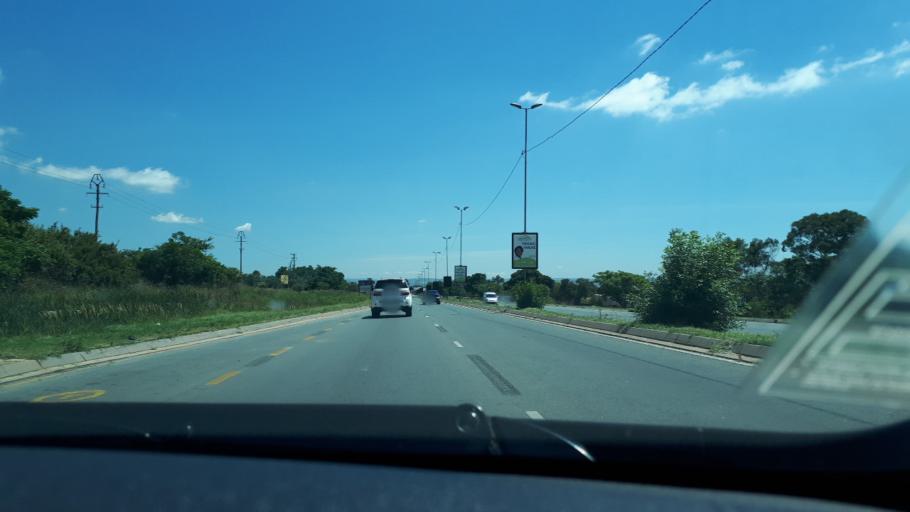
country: ZA
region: Gauteng
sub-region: West Rand District Municipality
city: Muldersdriseloop
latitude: -26.0536
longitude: 27.9556
